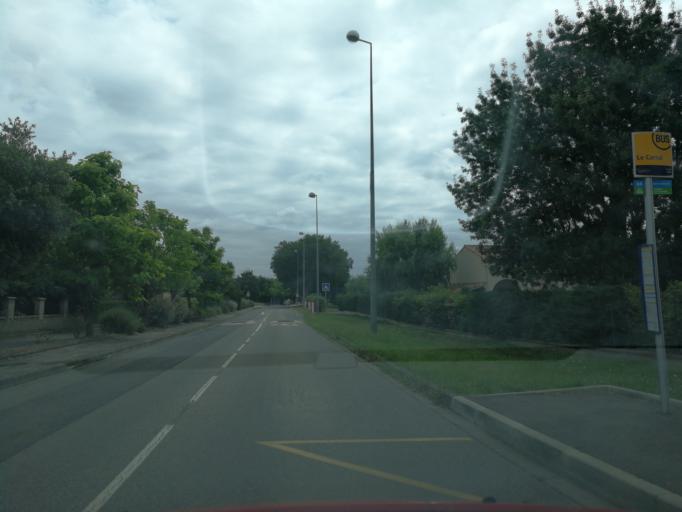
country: FR
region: Midi-Pyrenees
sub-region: Departement de la Haute-Garonne
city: Balma
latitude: 43.6181
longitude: 1.4958
